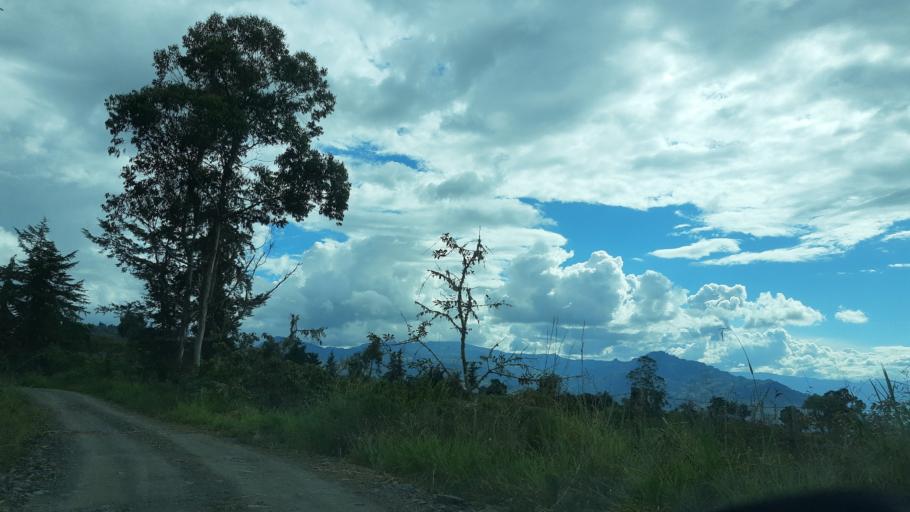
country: CO
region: Boyaca
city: Garagoa
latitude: 5.0329
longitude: -73.3320
